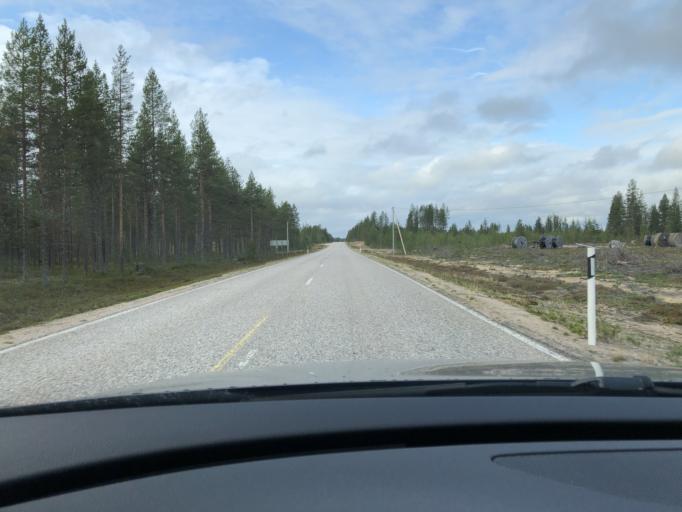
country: FI
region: Lapland
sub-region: Itae-Lappi
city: Posio
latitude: 66.0658
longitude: 28.0547
